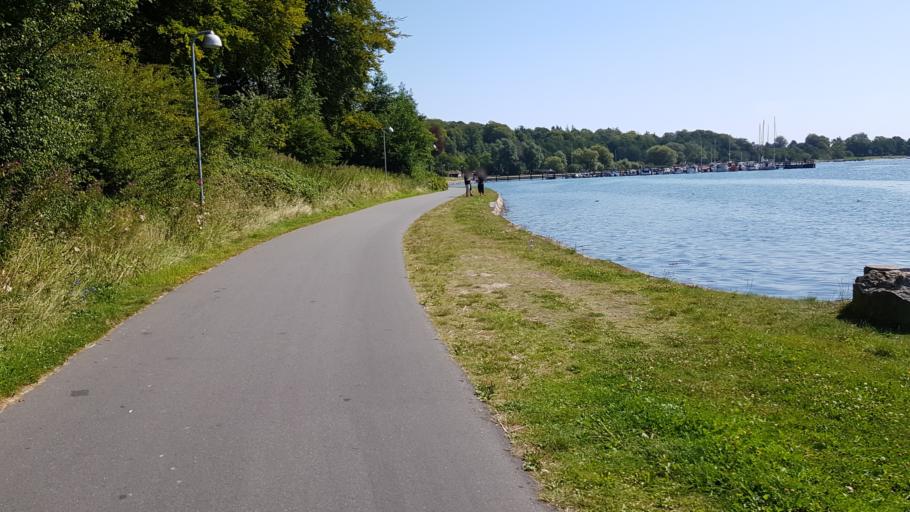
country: DK
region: South Denmark
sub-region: Svendborg Kommune
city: Vindeby
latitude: 55.0598
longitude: 10.6310
